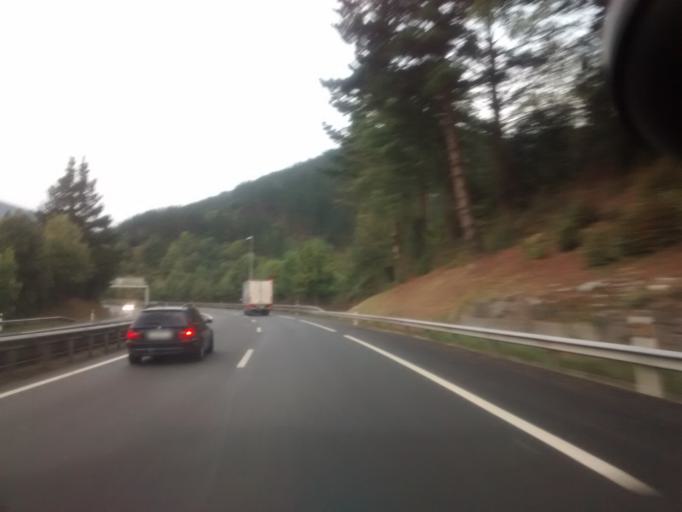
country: ES
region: Basque Country
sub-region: Provincia de Guipuzcoa
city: Mendaro
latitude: 43.2505
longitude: -2.3925
